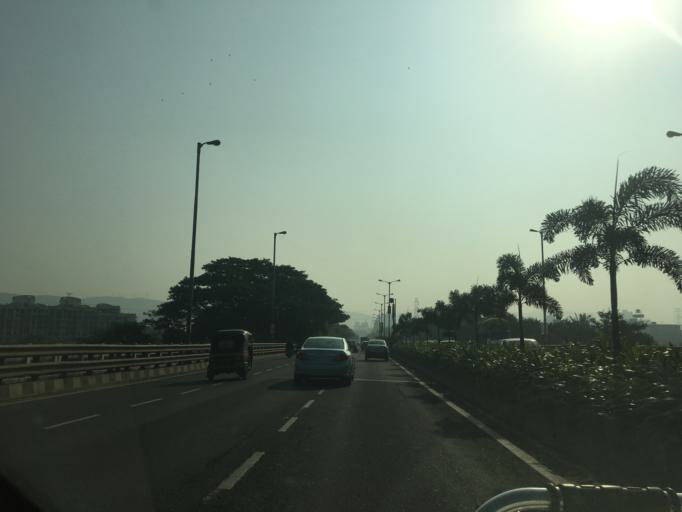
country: IN
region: Maharashtra
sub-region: Thane
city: Airoli
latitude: 19.1502
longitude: 72.9836
